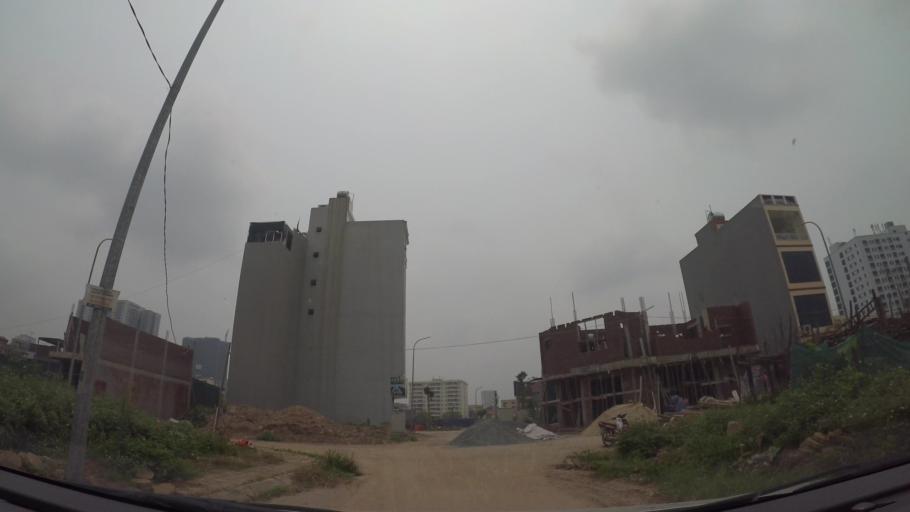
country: VN
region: Ha Noi
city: Ha Dong
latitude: 20.9770
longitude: 105.7699
